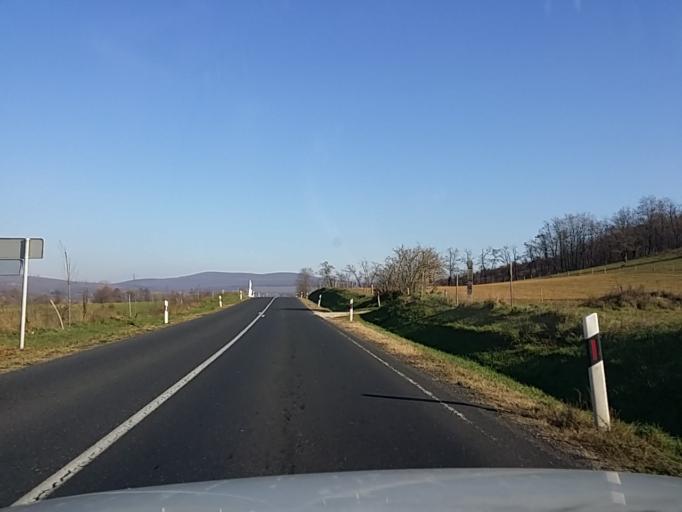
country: HU
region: Veszprem
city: Tapolca
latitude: 46.9113
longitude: 17.5339
